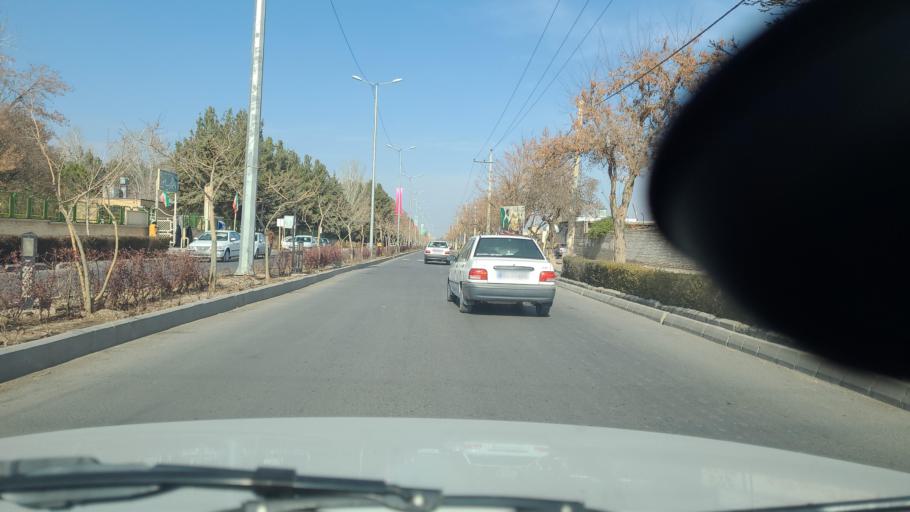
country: IR
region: Razavi Khorasan
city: Fariman
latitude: 35.6894
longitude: 59.8439
